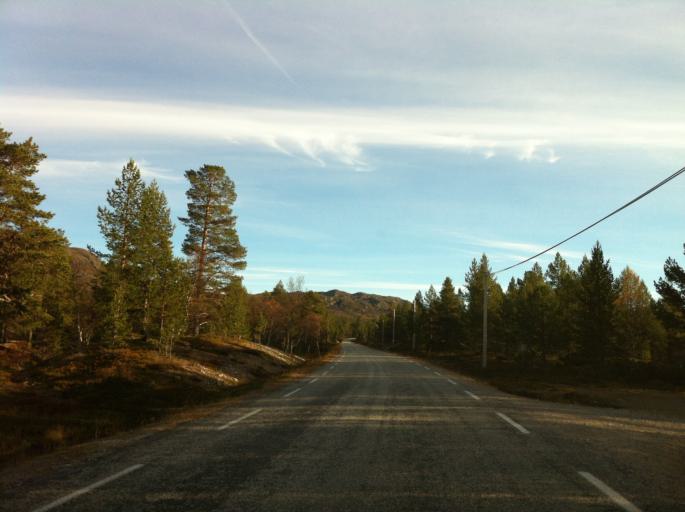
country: NO
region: Hedmark
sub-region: Engerdal
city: Engerdal
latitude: 62.1222
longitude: 12.0062
